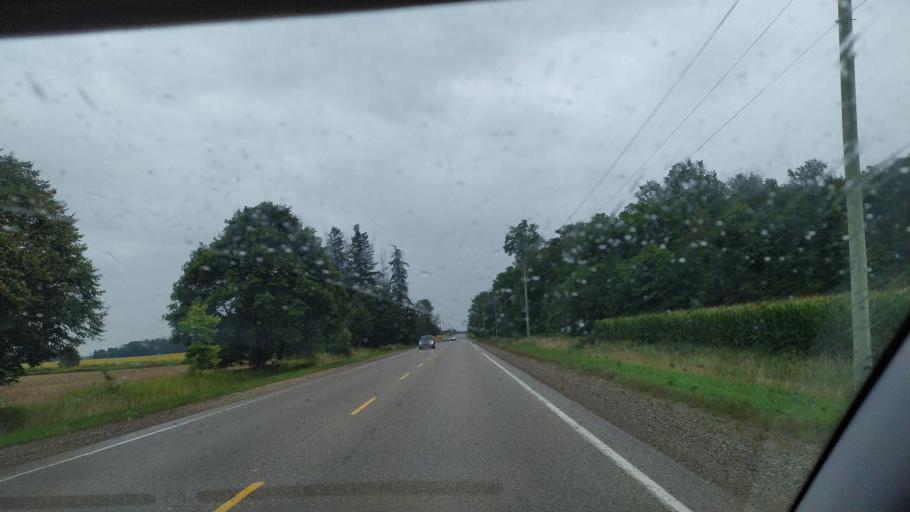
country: CA
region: Ontario
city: Kitchener
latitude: 43.3303
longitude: -80.6739
